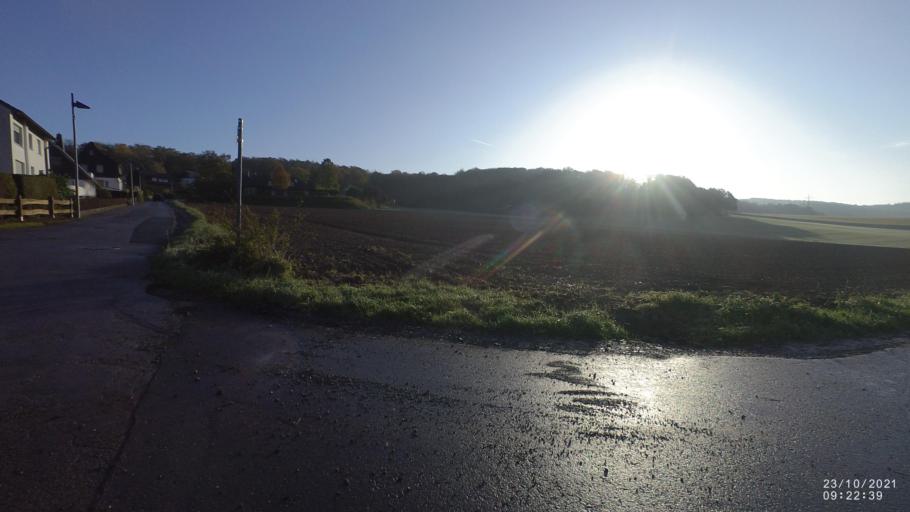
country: DE
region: North Rhine-Westphalia
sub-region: Regierungsbezirk Arnsberg
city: Menden
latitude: 51.4581
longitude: 7.7994
